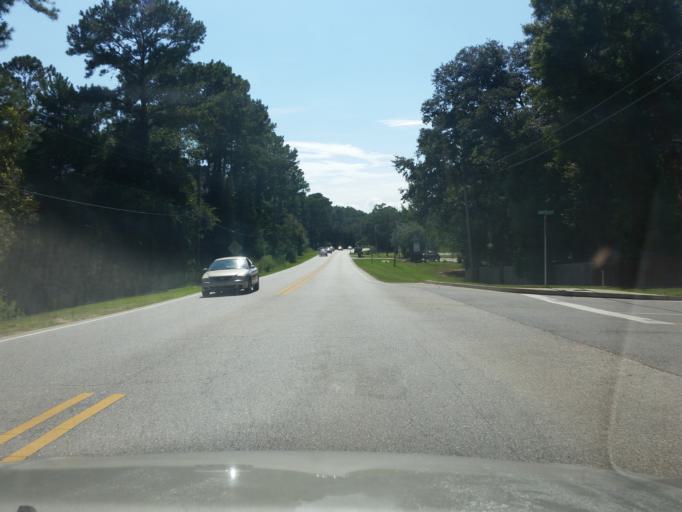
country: US
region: Alabama
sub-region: Baldwin County
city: Spanish Fort
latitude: 30.6740
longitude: -87.8753
